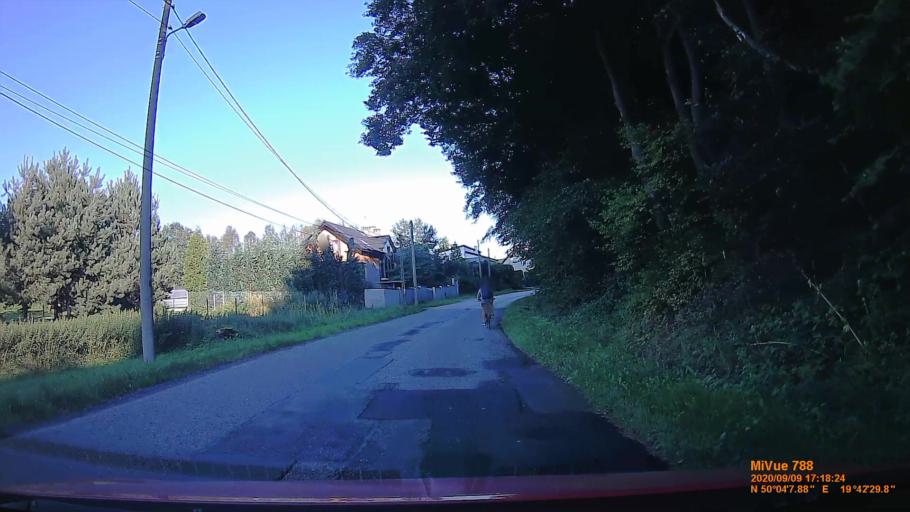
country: PL
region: Lesser Poland Voivodeship
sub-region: Powiat krakowski
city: Czulow
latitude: 50.0689
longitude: 19.7082
